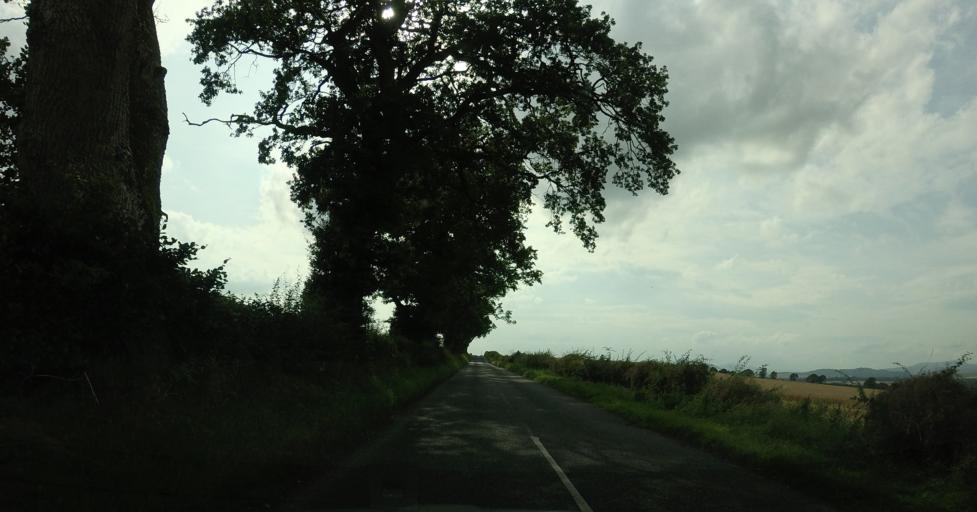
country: GB
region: Scotland
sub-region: Perth and Kinross
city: Auchterarder
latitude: 56.3734
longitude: -3.6806
